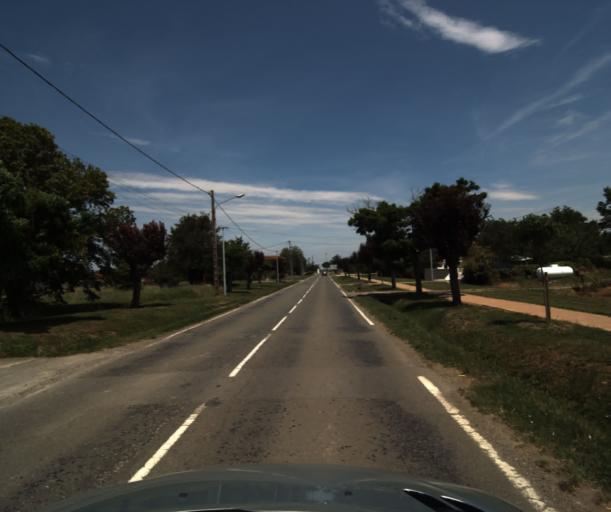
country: FR
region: Midi-Pyrenees
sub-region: Departement de la Haute-Garonne
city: Labastidette
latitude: 43.4648
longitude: 1.2492
